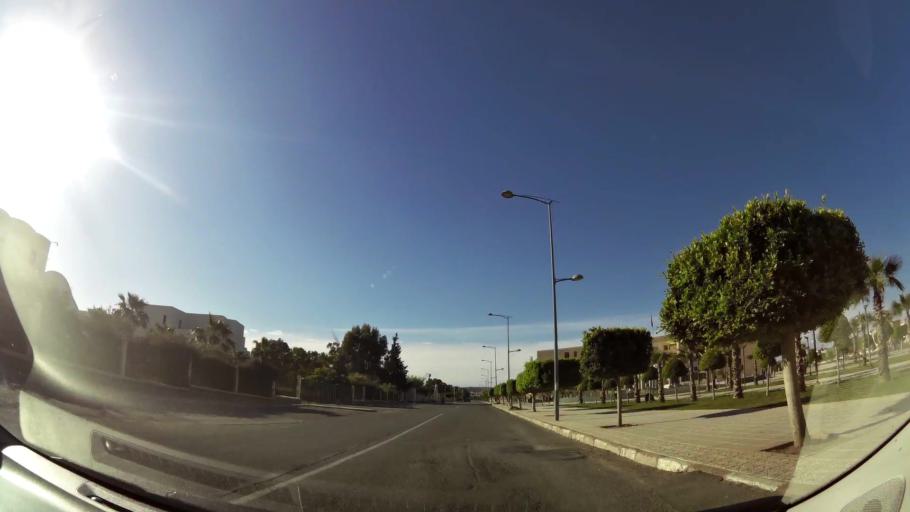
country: MA
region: Oriental
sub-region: Oujda-Angad
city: Oujda
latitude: 34.6617
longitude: -1.9114
